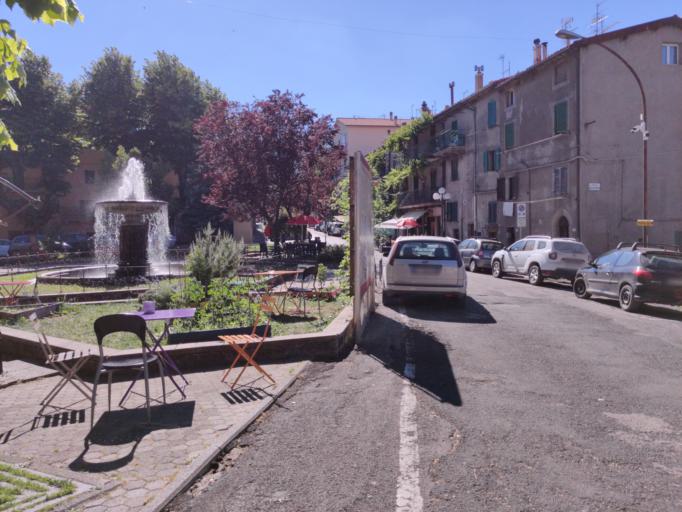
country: IT
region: Tuscany
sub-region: Provincia di Siena
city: Abbadia San Salvatore
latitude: 42.8817
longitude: 11.6778
